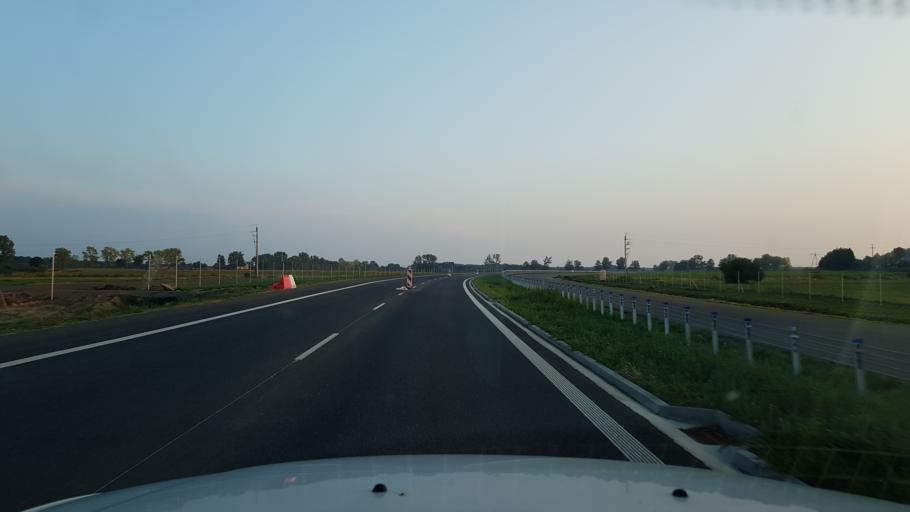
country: PL
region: West Pomeranian Voivodeship
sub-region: Powiat goleniowski
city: Nowogard
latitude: 53.7202
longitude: 15.1957
